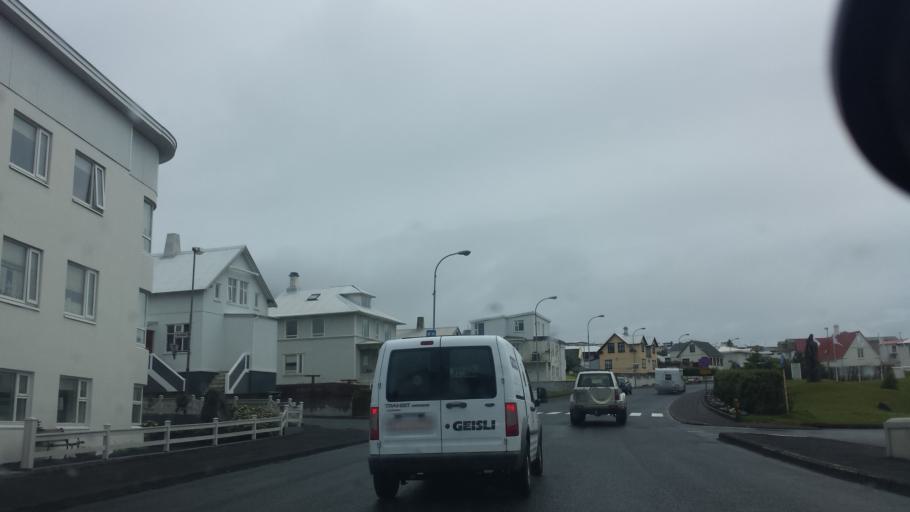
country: IS
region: South
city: Vestmannaeyjar
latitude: 63.4401
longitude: -20.2665
